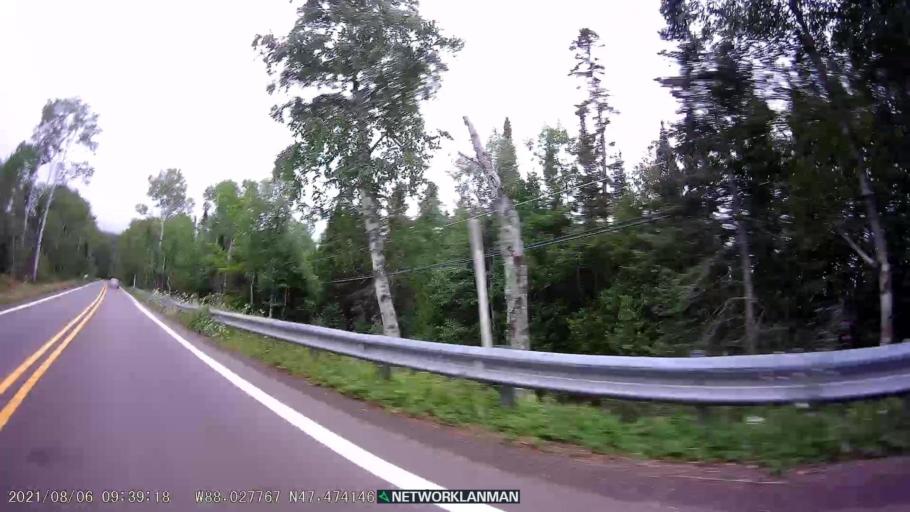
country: US
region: Michigan
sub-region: Keweenaw County
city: Eagle River
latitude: 47.4740
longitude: -88.0278
